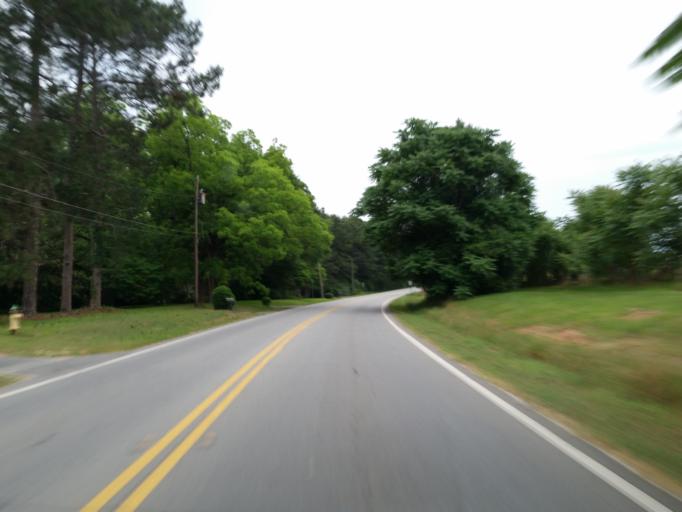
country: US
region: Georgia
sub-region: Dooly County
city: Vienna
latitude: 32.0868
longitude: -83.7949
